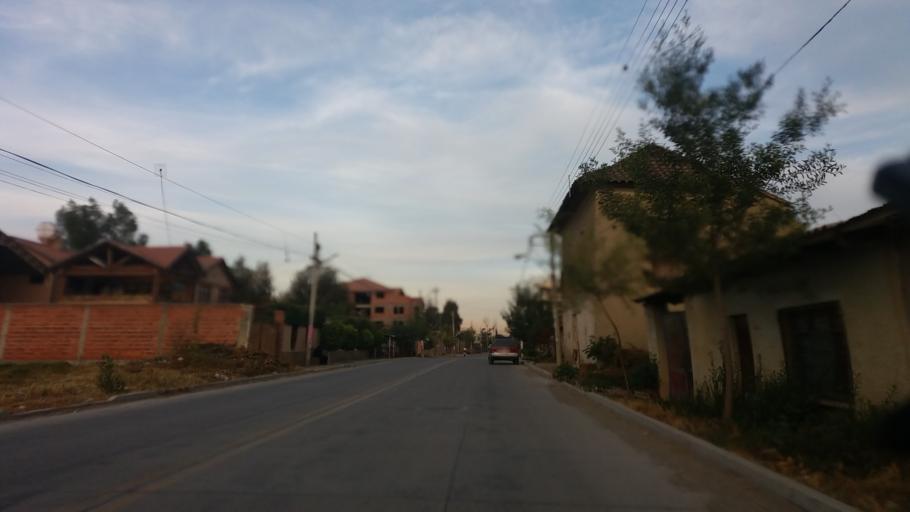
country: BO
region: Cochabamba
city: Cochabamba
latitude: -17.3685
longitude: -66.2107
